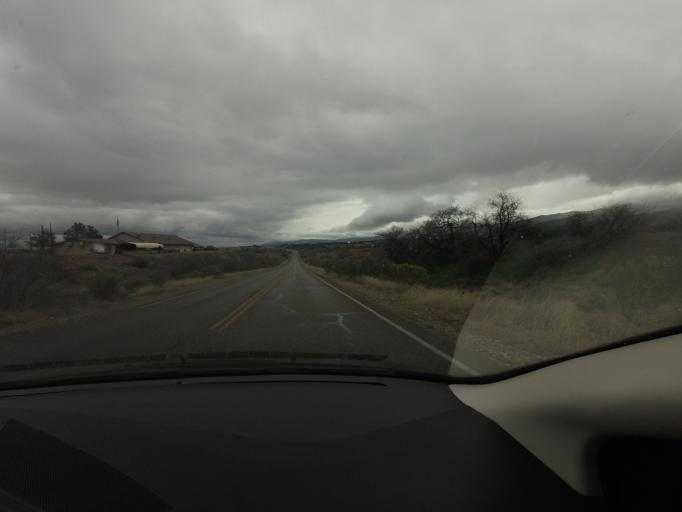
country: US
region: Arizona
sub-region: Yavapai County
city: Clarkdale
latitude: 34.7586
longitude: -112.0380
